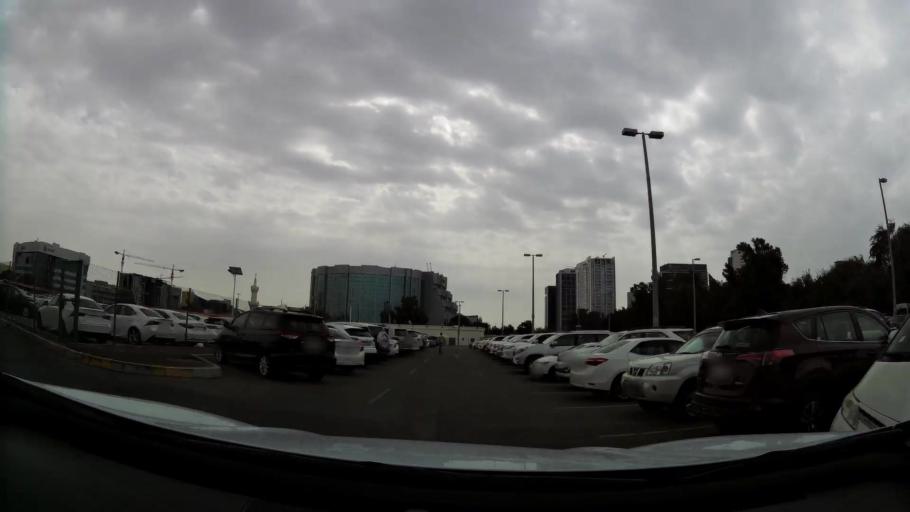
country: AE
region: Abu Dhabi
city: Abu Dhabi
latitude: 24.4248
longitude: 54.4456
